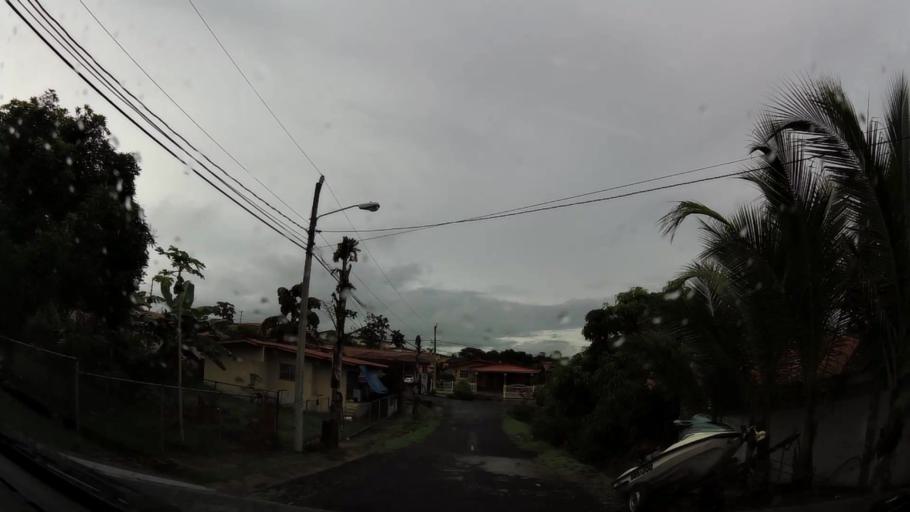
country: PA
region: Veraguas
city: Santiago de Veraguas
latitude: 8.0838
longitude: -80.9864
